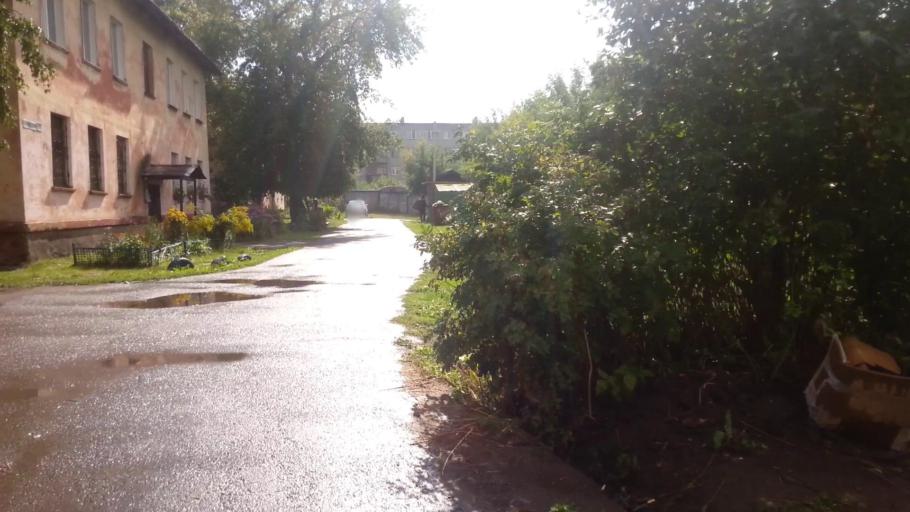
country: RU
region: Altai Krai
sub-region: Gorod Barnaulskiy
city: Barnaul
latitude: 53.3474
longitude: 83.7576
